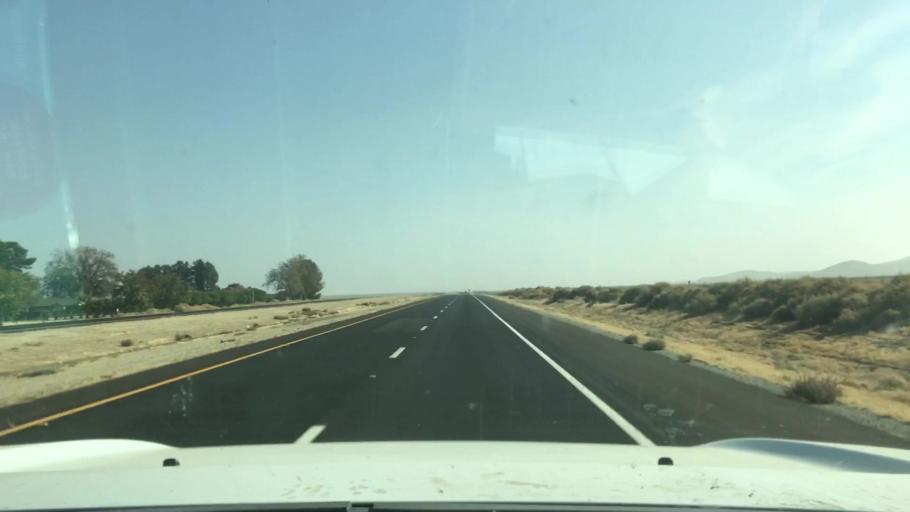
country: US
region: California
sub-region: Kern County
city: Lost Hills
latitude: 35.6390
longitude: -120.0161
